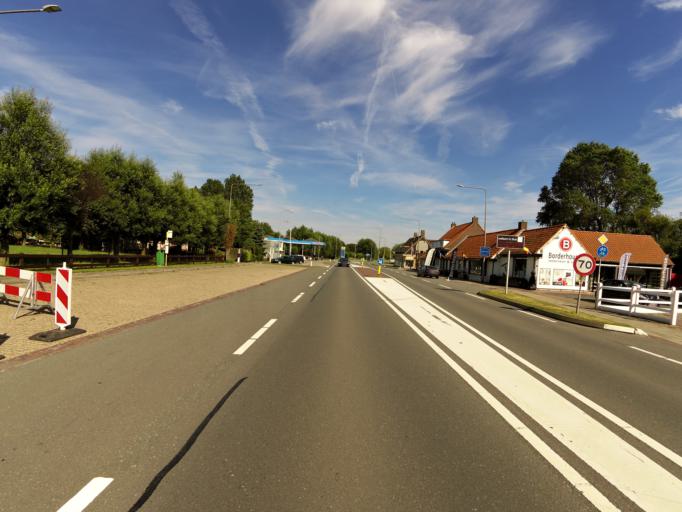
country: NL
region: Zeeland
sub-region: Gemeente Sluis
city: Sluis
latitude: 51.3146
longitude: 3.3592
